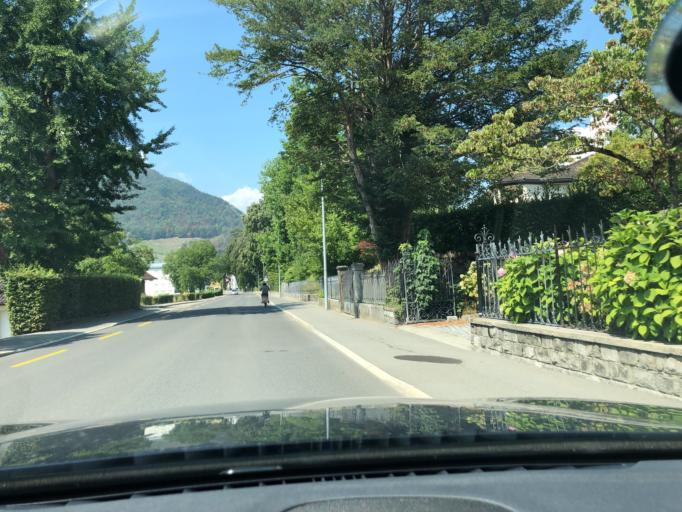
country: CH
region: Schwyz
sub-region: Bezirk Schwyz
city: Schwyz
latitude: 47.0223
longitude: 8.6461
